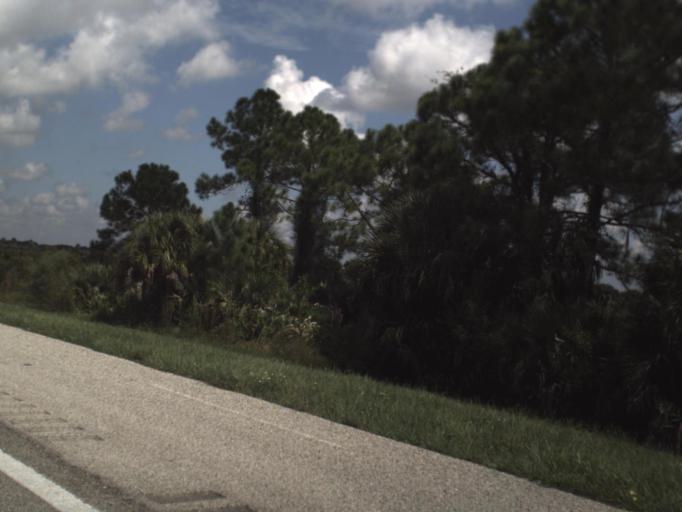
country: US
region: Florida
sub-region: Sarasota County
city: Osprey
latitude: 27.1942
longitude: -82.4364
